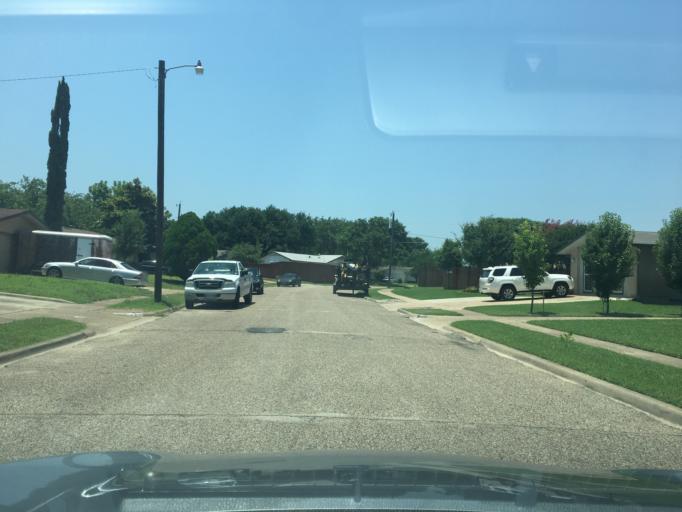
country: US
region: Texas
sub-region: Dallas County
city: Garland
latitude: 32.9128
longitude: -96.6868
